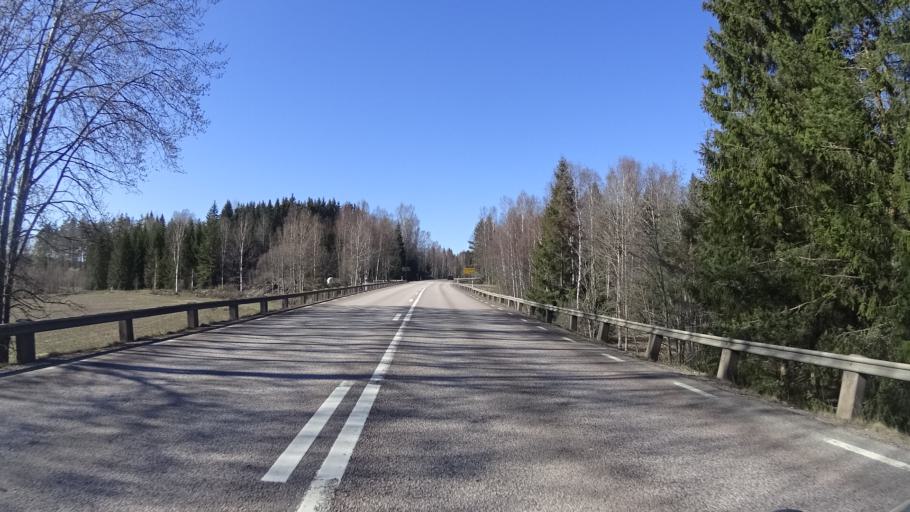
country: SE
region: Vaermland
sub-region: Karlstads Kommun
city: Edsvalla
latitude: 59.5633
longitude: 13.0286
